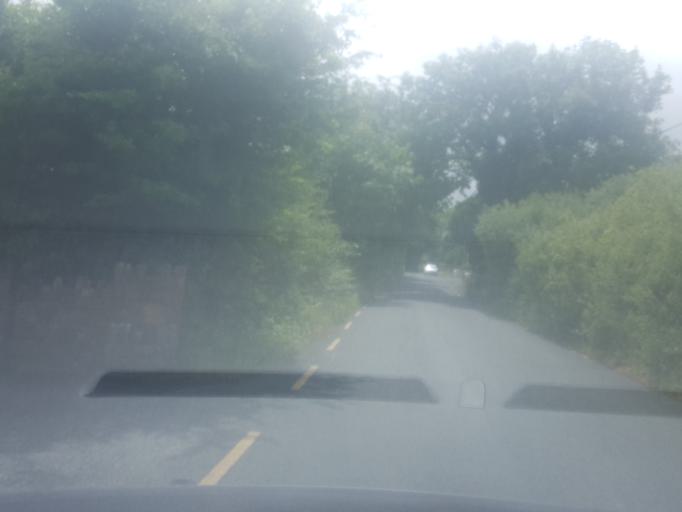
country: IE
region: Munster
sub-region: Ciarrai
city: Cill Airne
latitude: 52.0928
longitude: -9.4782
